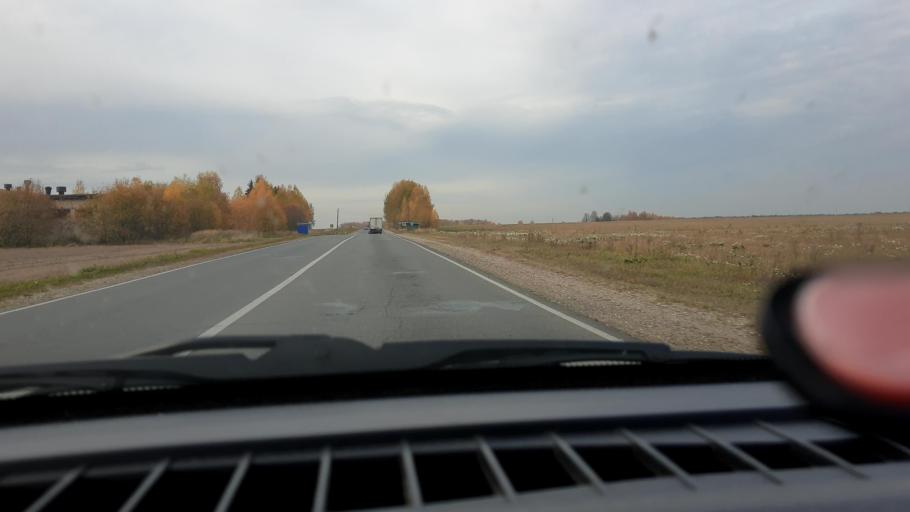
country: RU
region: Nizjnij Novgorod
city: Gorodets
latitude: 56.6234
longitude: 43.5494
